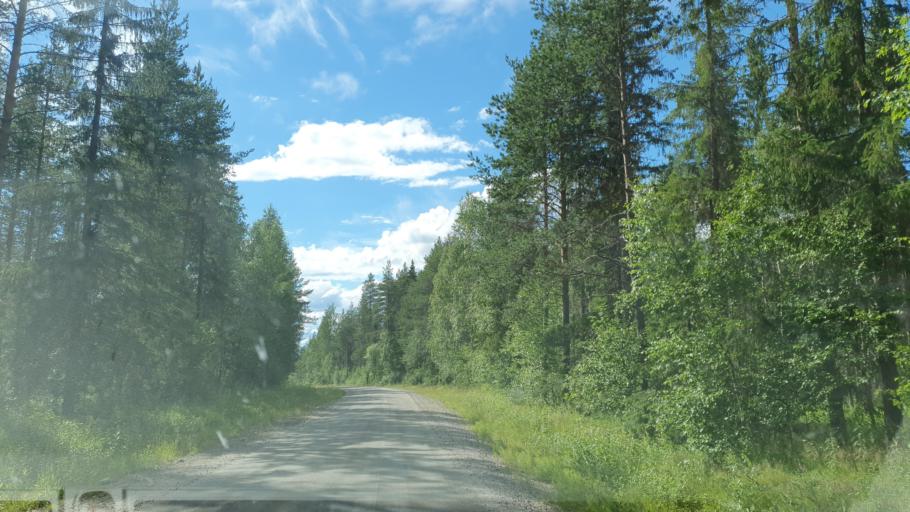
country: FI
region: Kainuu
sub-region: Kehys-Kainuu
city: Kuhmo
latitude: 64.1624
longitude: 29.8451
